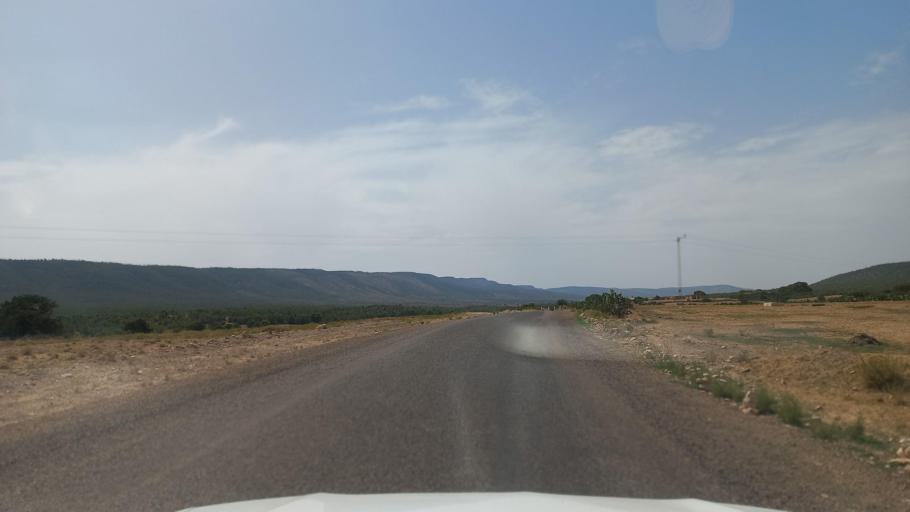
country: TN
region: Al Qasrayn
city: Sbiba
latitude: 35.3898
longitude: 8.9480
